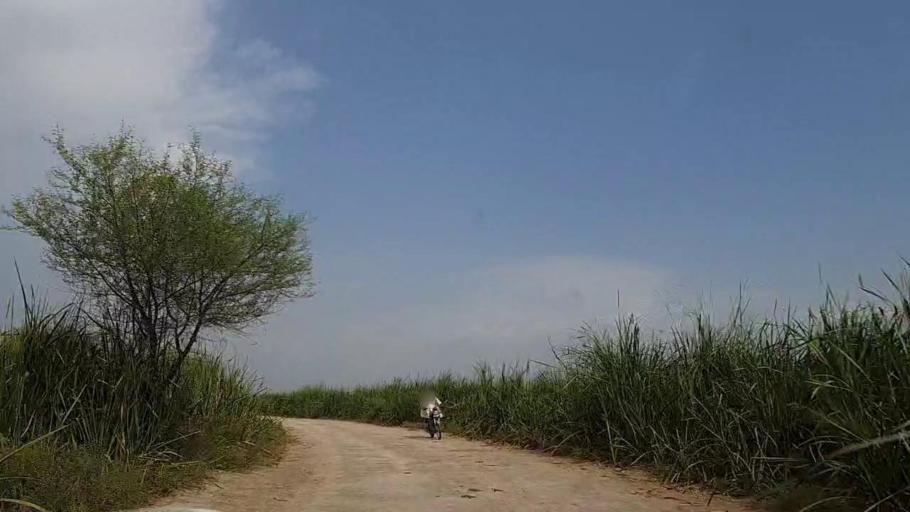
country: PK
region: Sindh
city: Khanpur
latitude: 27.8363
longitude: 69.4944
